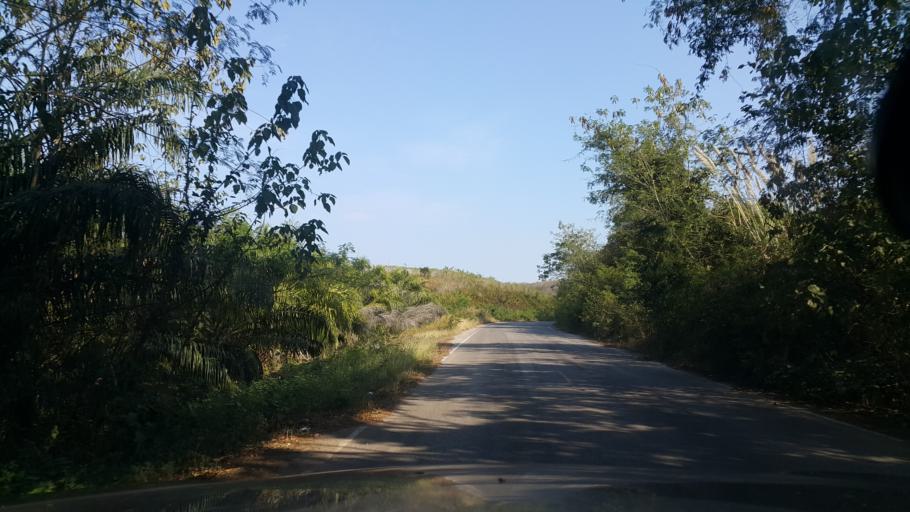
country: TH
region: Loei
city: Chiang Khan
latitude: 17.8324
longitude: 101.6270
